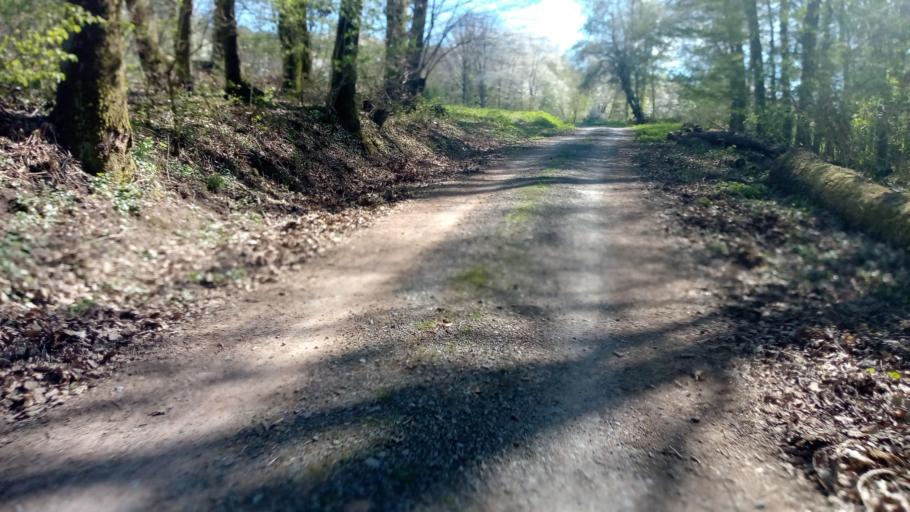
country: DE
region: Bavaria
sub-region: Regierungsbezirk Unterfranken
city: Hasloch
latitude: 49.7975
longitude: 9.5033
